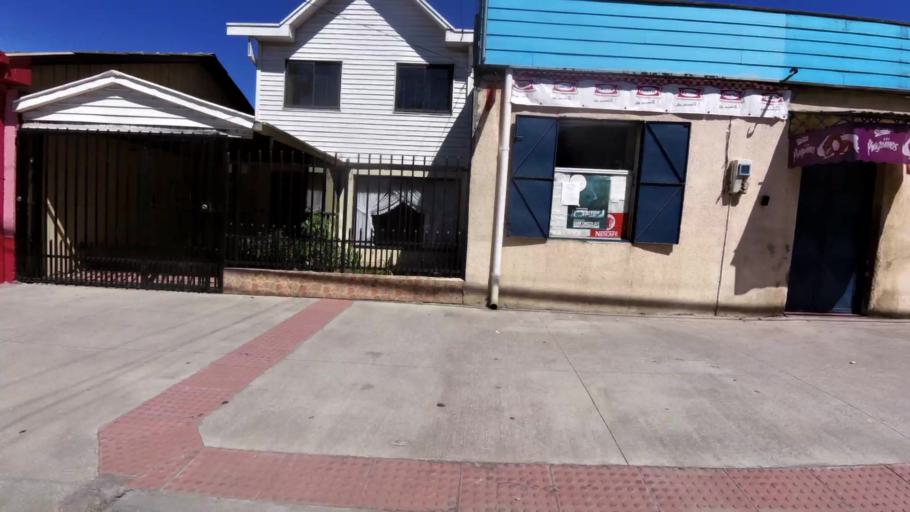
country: CL
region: Biobio
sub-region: Provincia de Concepcion
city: Penco
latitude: -36.7392
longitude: -73.0002
